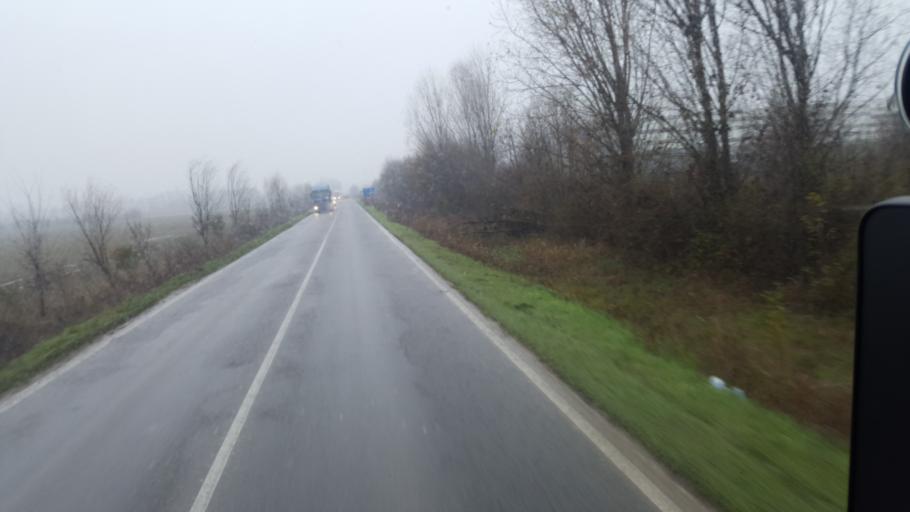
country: IT
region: Lombardy
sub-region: Provincia di Pavia
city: Landriano
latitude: 45.3016
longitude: 9.2582
